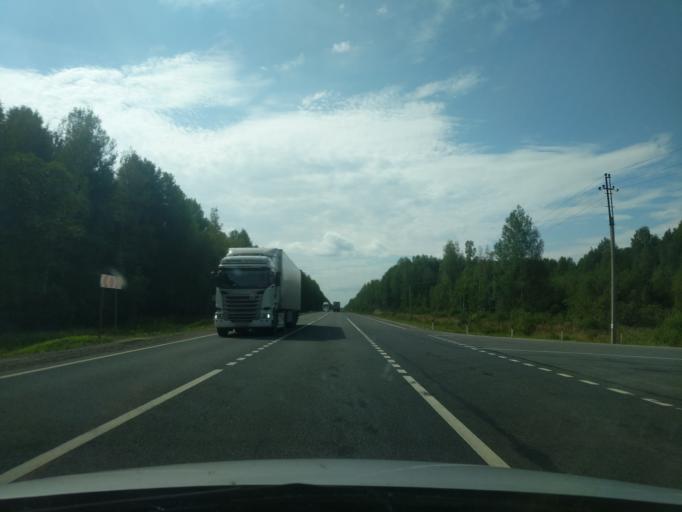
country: RU
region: Kostroma
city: Kadyy
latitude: 57.8158
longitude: 43.2333
